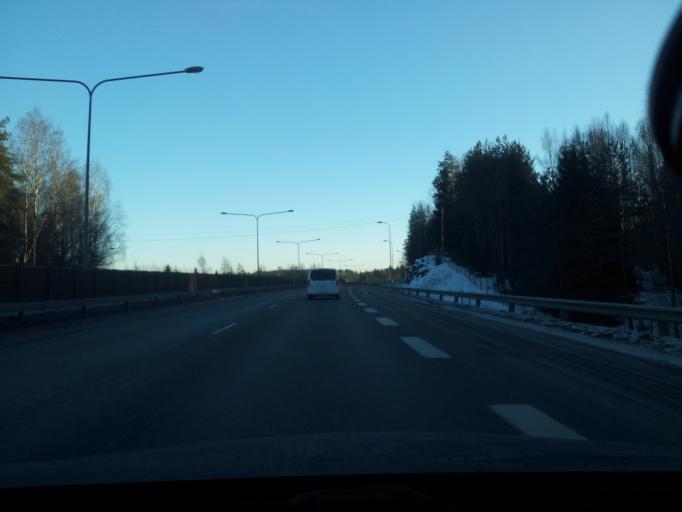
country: FI
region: Uusimaa
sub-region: Helsinki
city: Espoo
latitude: 60.2403
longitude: 24.5764
